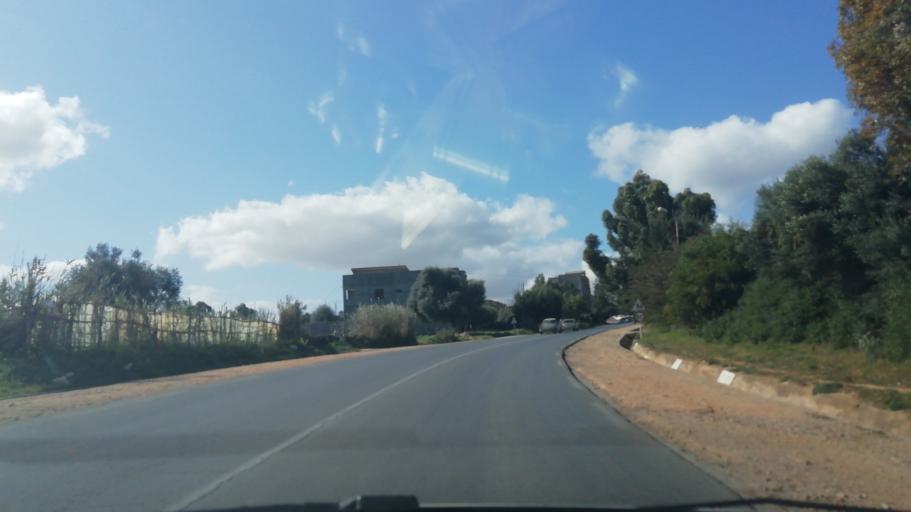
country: DZ
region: Relizane
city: Mazouna
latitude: 36.2860
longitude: 0.6462
